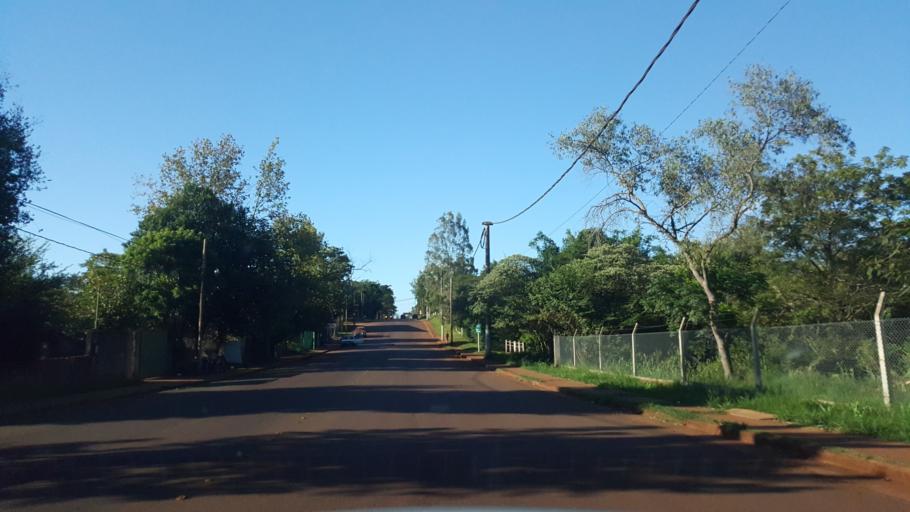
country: AR
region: Misiones
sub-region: Departamento de Capital
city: Posadas
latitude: -27.4208
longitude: -55.9580
